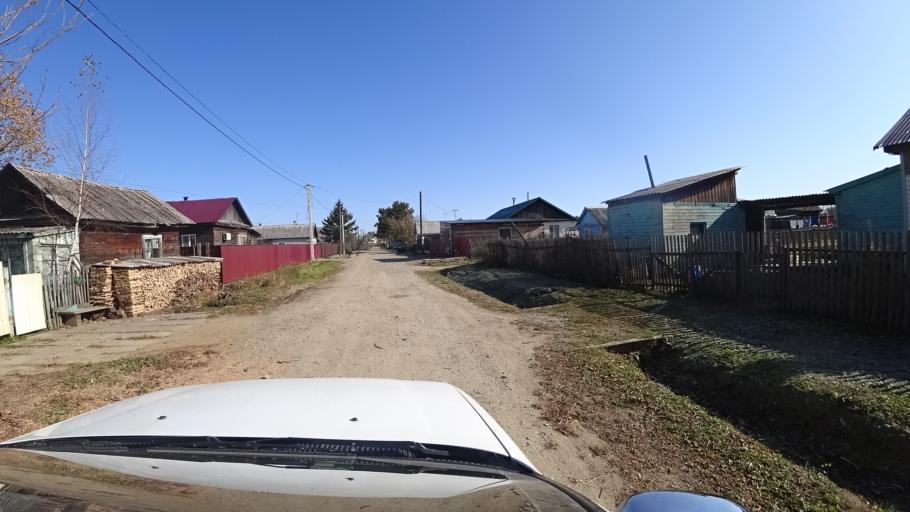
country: RU
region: Primorskiy
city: Dal'nerechensk
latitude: 45.9076
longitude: 133.8049
